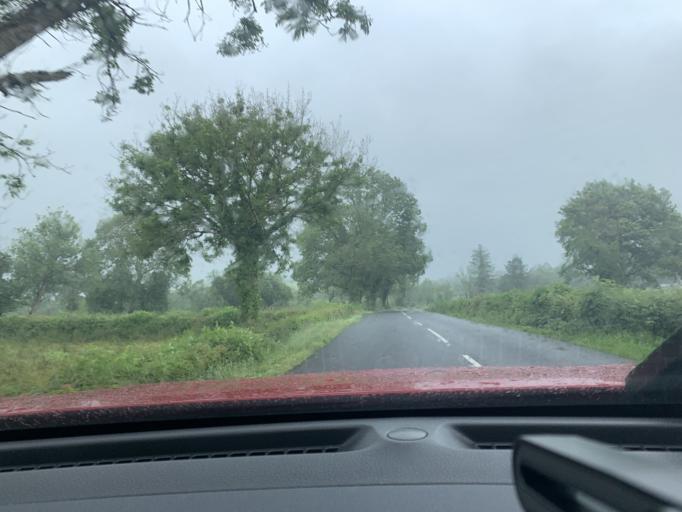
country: GB
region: Northern Ireland
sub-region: Fermanagh District
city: Enniskillen
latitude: 54.2929
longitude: -7.6971
